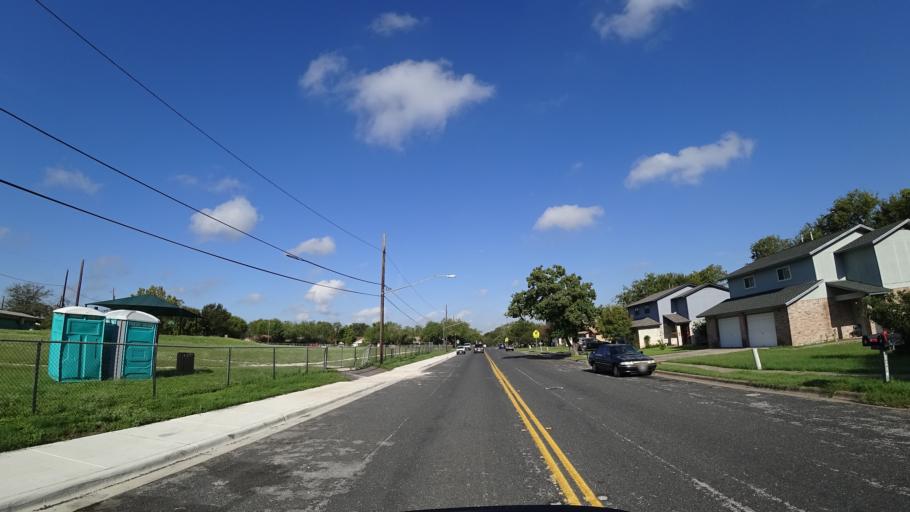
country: US
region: Texas
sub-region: Travis County
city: Rollingwood
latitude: 30.2112
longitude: -97.8049
